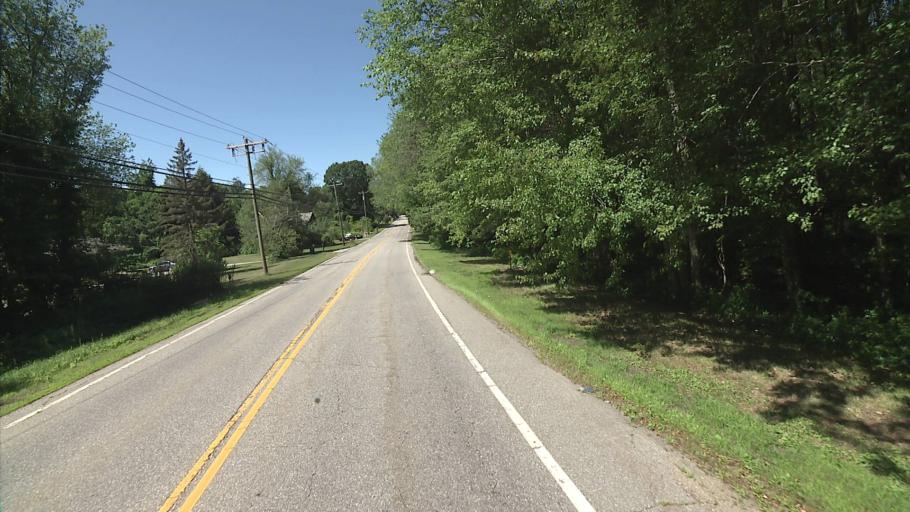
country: US
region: Connecticut
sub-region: Windham County
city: Willimantic
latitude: 41.6876
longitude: -72.2304
